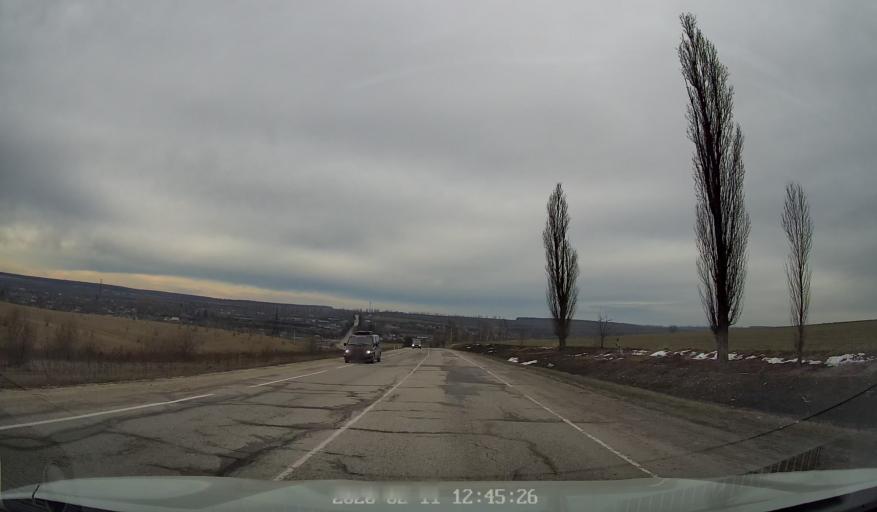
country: MD
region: Raionul Edinet
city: Edinet
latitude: 48.2580
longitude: 27.1963
